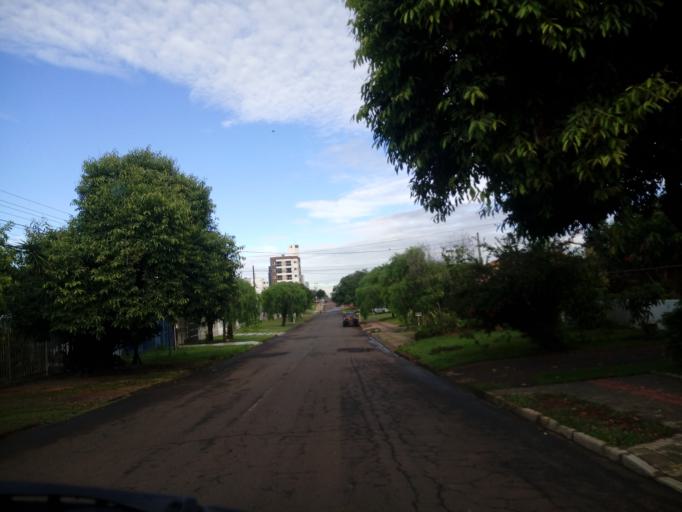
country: BR
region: Santa Catarina
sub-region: Chapeco
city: Chapeco
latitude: -27.1073
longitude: -52.6259
